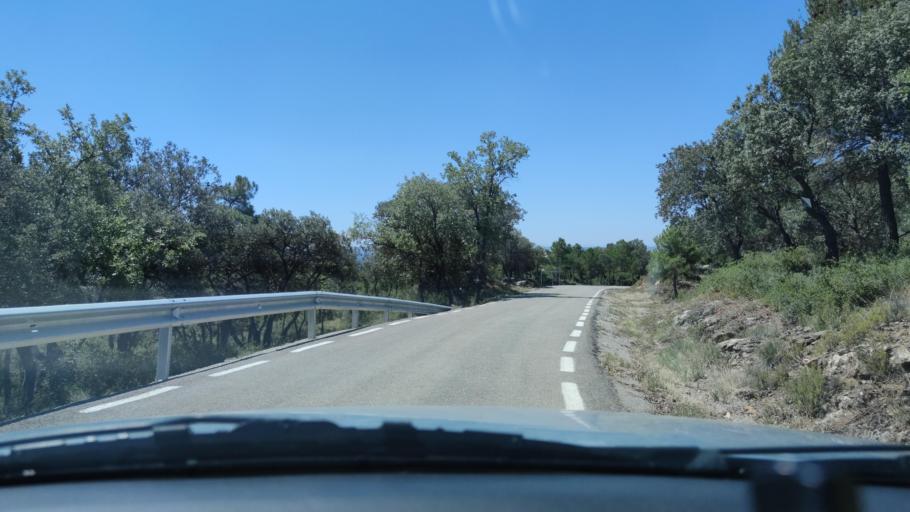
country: ES
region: Catalonia
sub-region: Provincia de Lleida
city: Tora de Riubregos
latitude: 41.8657
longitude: 1.4349
